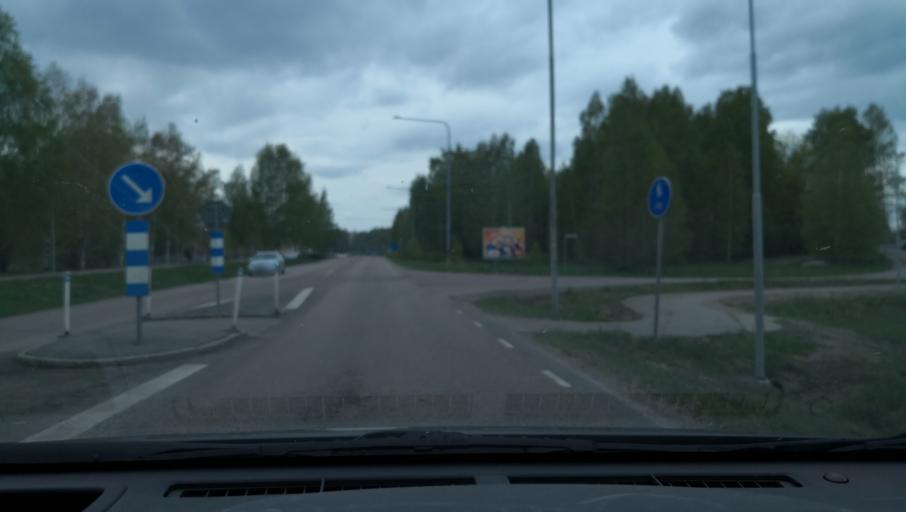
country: SE
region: Dalarna
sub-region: Avesta Kommun
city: Avesta
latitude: 60.1388
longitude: 16.2011
